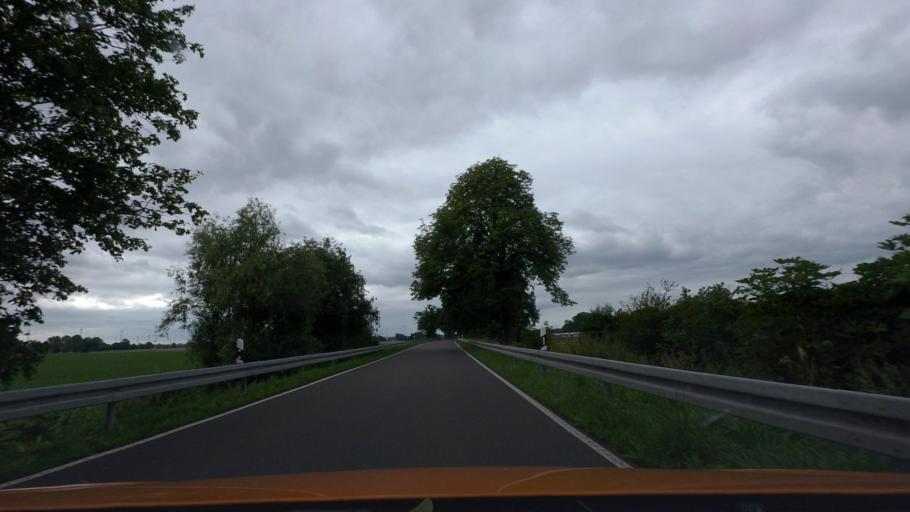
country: DE
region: Brandenburg
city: Bliesdorf
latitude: 52.7298
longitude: 14.1989
